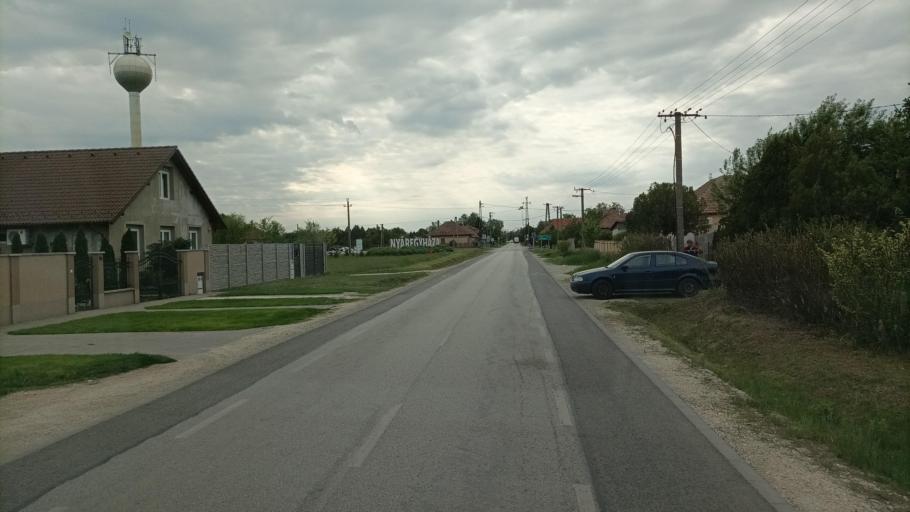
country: HU
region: Pest
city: Nyaregyhaza
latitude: 47.2656
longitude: 19.4994
